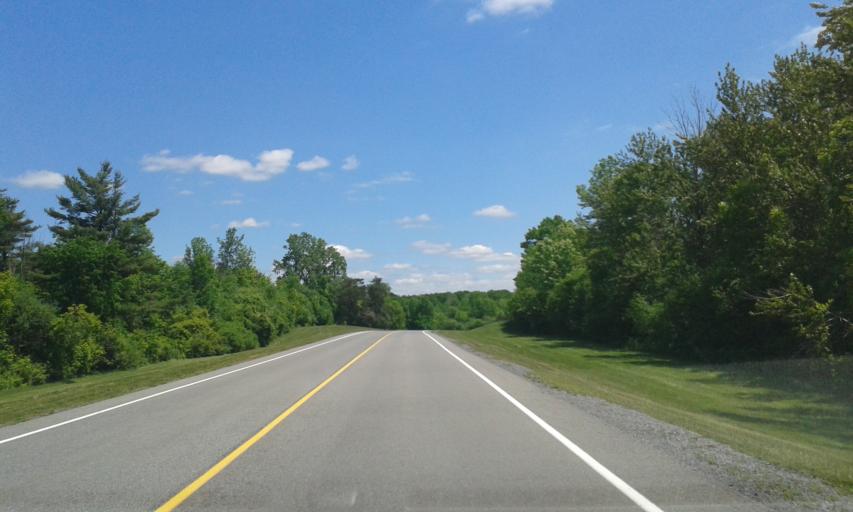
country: US
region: New York
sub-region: St. Lawrence County
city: Massena
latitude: 44.9950
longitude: -74.9451
